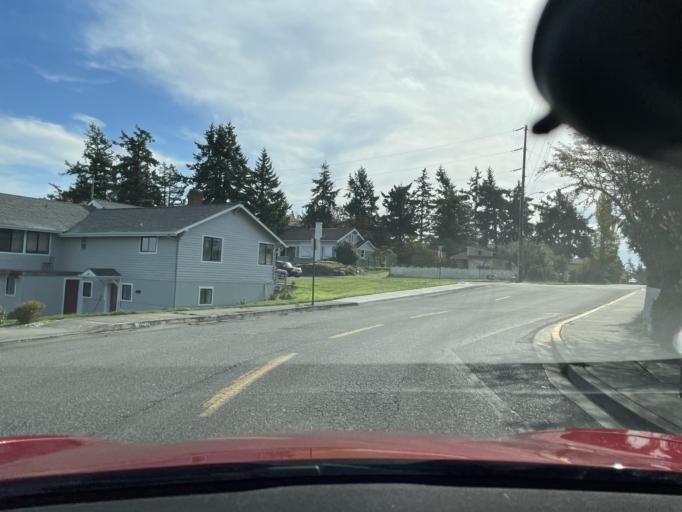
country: US
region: Washington
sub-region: San Juan County
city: Friday Harbor
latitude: 48.5318
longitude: -123.0193
